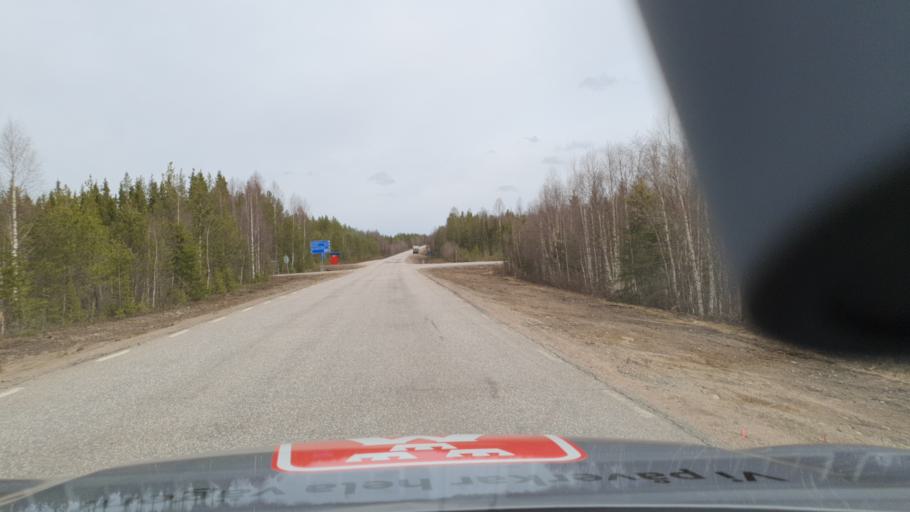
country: SE
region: Norrbotten
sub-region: Pajala Kommun
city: Pajala
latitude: 66.9174
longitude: 23.1451
